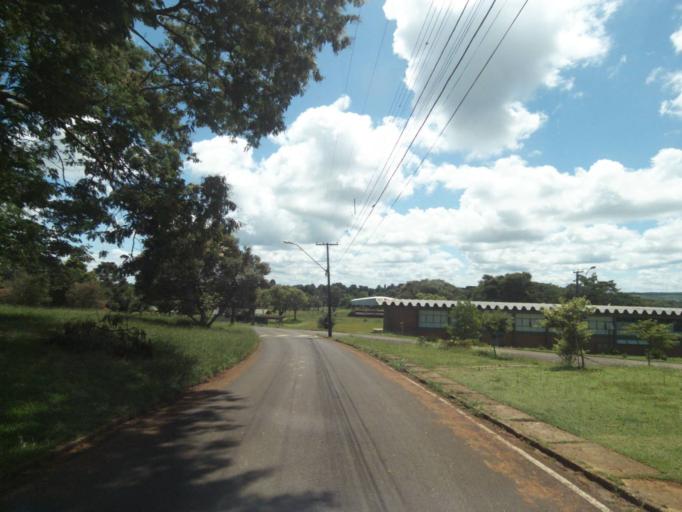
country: BR
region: Parana
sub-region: Chopinzinho
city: Chopinzinho
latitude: -25.7940
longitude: -52.0883
